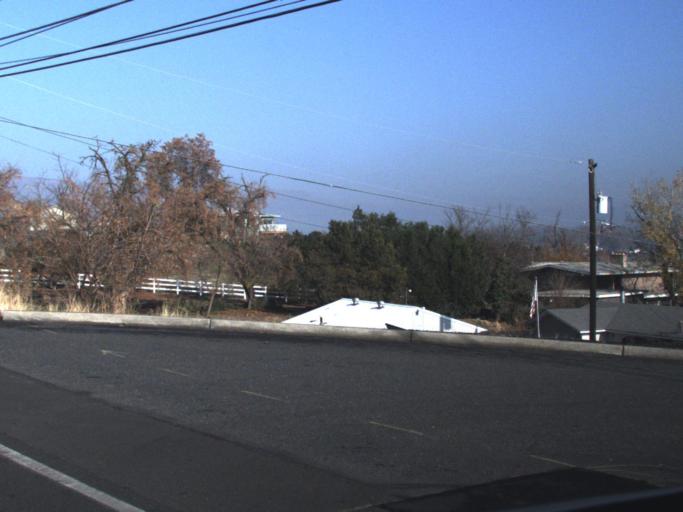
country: US
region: Washington
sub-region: Asotin County
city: Clarkston
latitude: 46.3987
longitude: -117.0443
